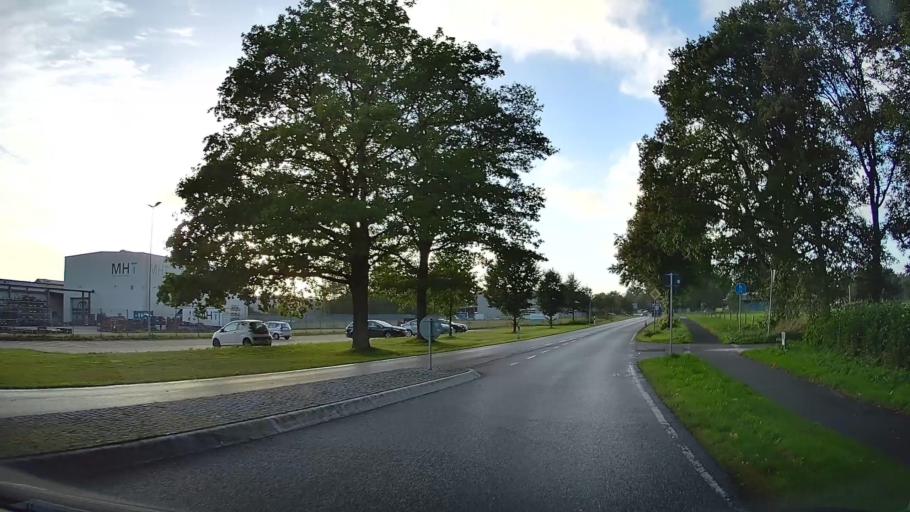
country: DE
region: Schleswig-Holstein
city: Horst
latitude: 53.8009
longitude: 9.6605
